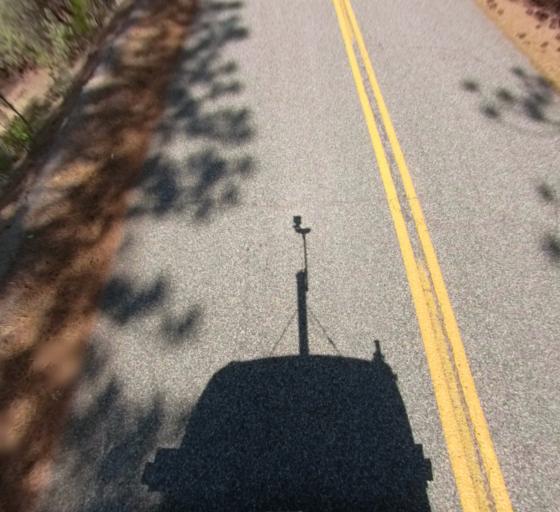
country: US
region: California
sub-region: Madera County
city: Oakhurst
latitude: 37.3820
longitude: -119.3593
